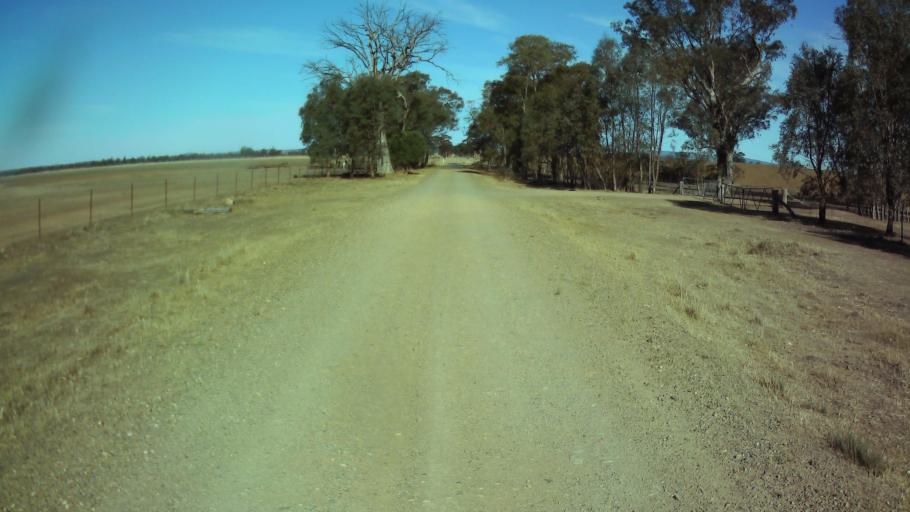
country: AU
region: New South Wales
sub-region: Weddin
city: Grenfell
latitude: -33.6582
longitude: 148.0994
